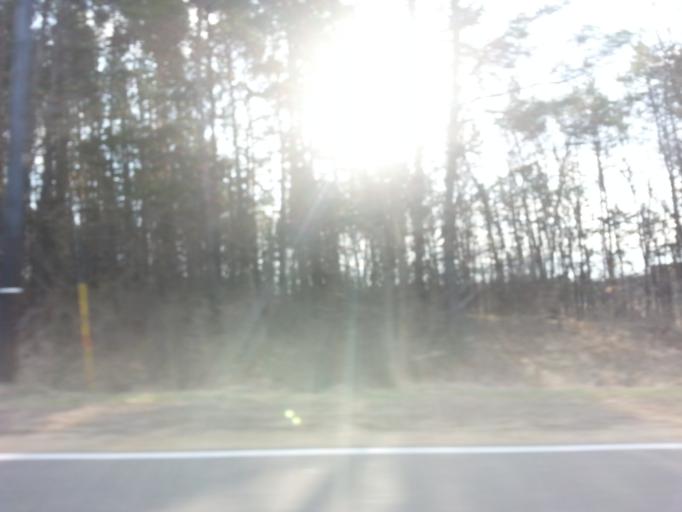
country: US
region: Minnesota
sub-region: Washington County
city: Afton
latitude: 44.9359
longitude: -92.8428
